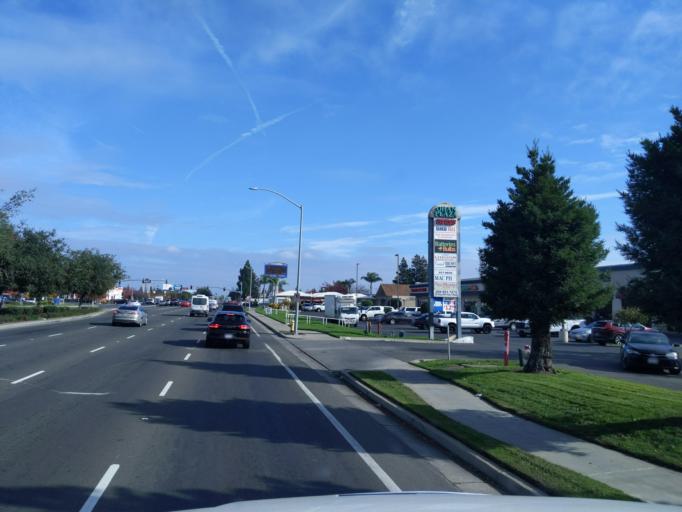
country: US
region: California
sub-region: San Joaquin County
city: Morada
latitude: 38.0210
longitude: -121.2738
